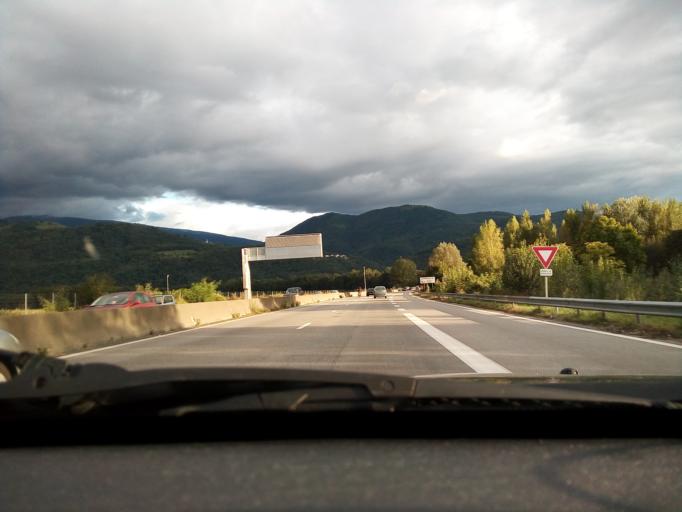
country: FR
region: Rhone-Alpes
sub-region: Departement de l'Isere
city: Gieres
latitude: 45.1969
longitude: 5.7813
